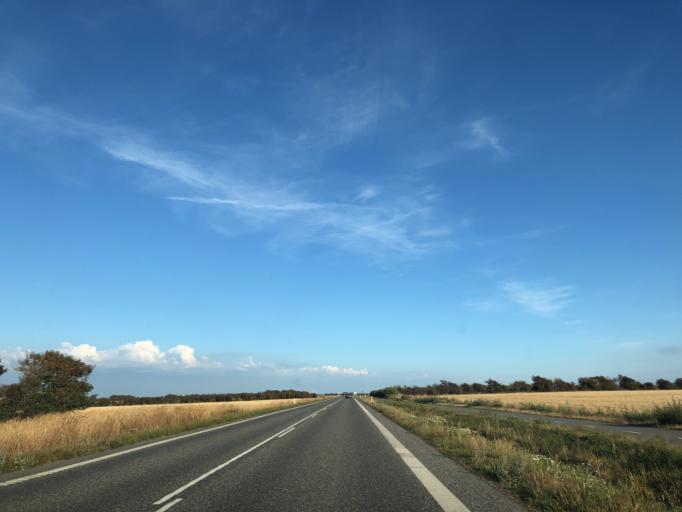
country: DK
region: Central Jutland
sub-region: Ringkobing-Skjern Kommune
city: Ringkobing
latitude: 56.1200
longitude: 8.1661
